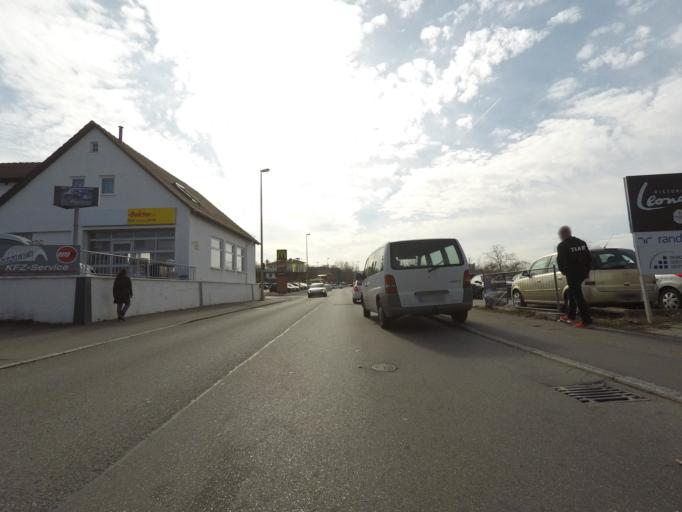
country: DE
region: Baden-Wuerttemberg
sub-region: Tuebingen Region
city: Reutlingen
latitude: 48.5029
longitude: 9.2157
